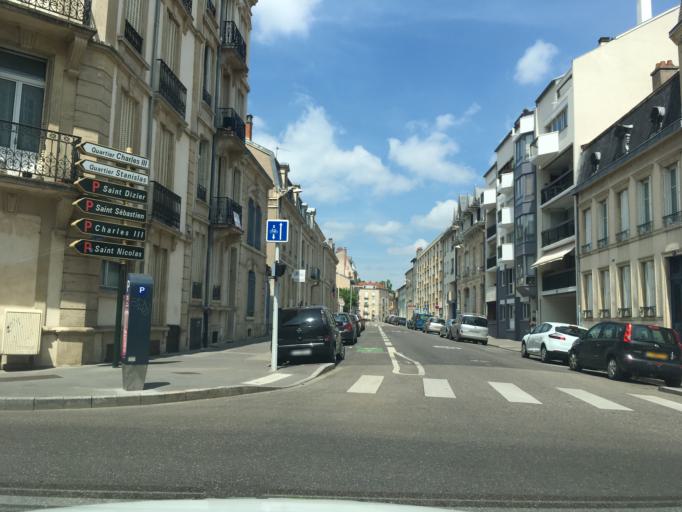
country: FR
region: Lorraine
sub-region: Departement de Meurthe-et-Moselle
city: Nancy
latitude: 48.6911
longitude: 6.1910
